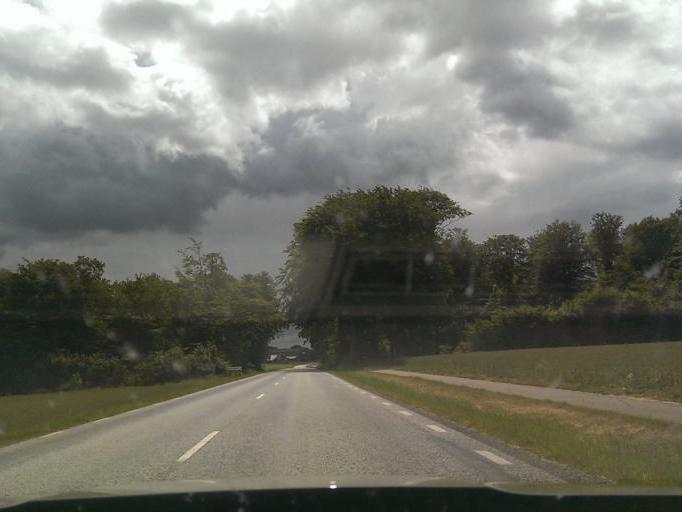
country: SE
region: Skane
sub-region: Eslovs Kommun
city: Stehag
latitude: 55.9532
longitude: 13.3443
